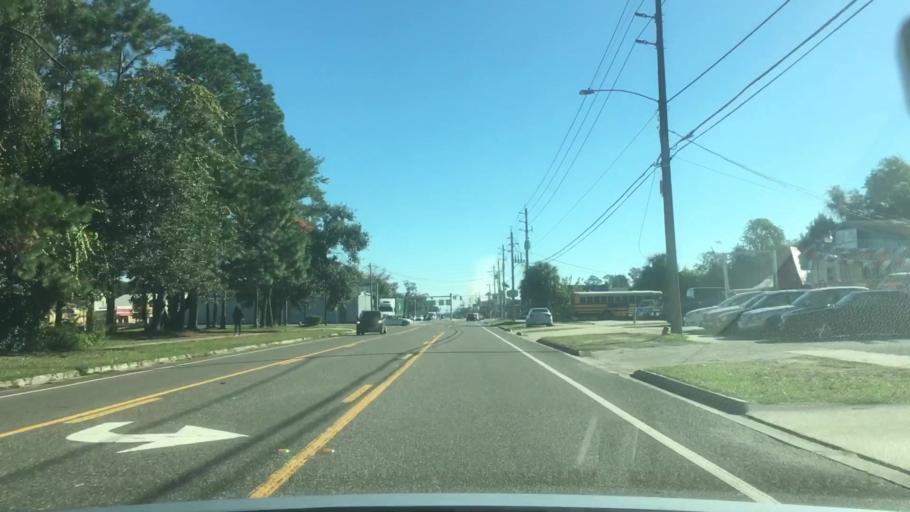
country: US
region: Florida
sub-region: Duval County
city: Jacksonville
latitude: 30.4298
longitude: -81.6743
